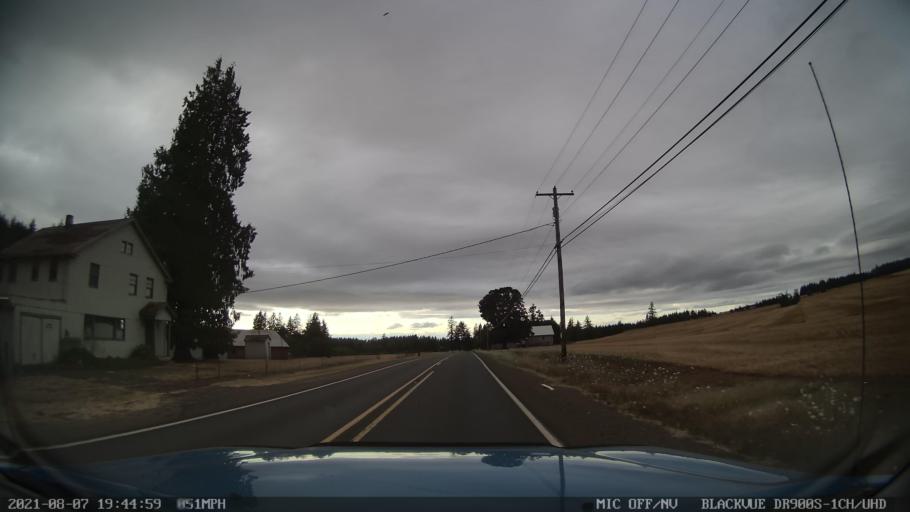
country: US
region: Oregon
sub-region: Marion County
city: Silverton
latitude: 44.9440
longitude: -122.6904
